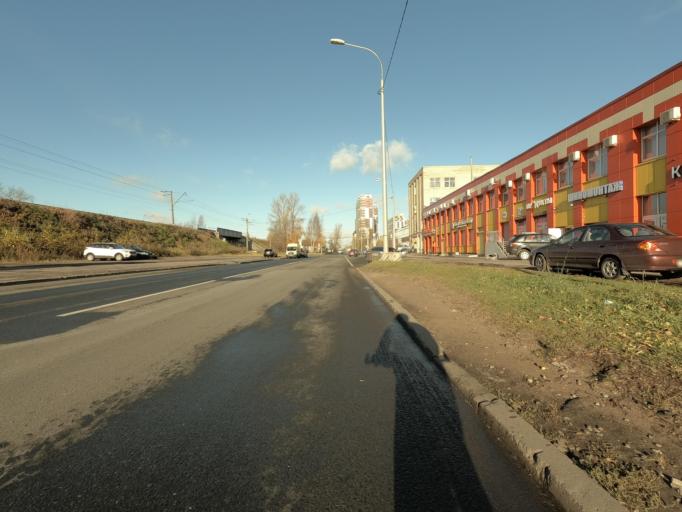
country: RU
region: St.-Petersburg
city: Krasnogvargeisky
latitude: 59.9520
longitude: 30.4476
